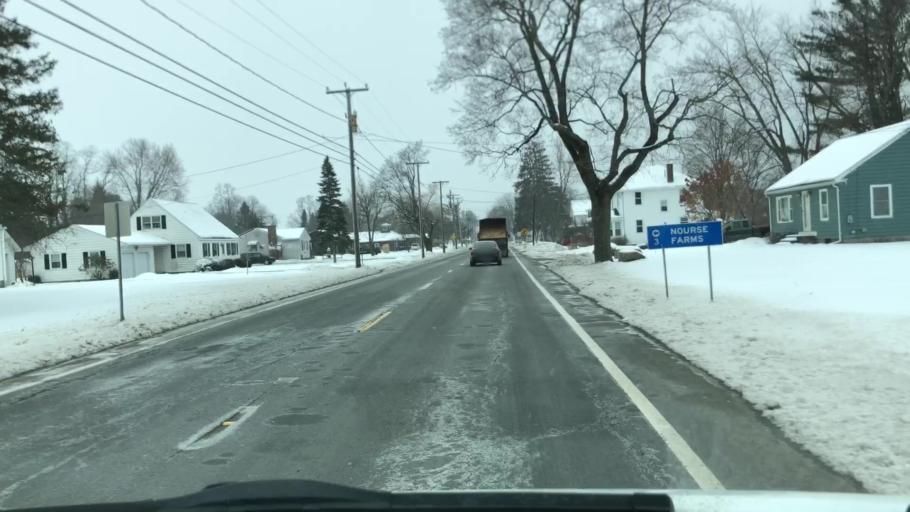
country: US
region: Massachusetts
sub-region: Franklin County
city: Whately
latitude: 42.4131
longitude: -72.6224
